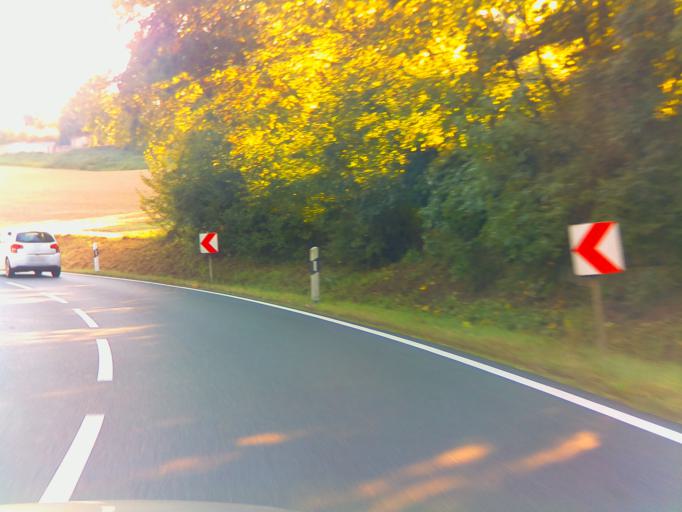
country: DE
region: Bavaria
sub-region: Regierungsbezirk Unterfranken
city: Gaukonigshofen
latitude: 49.6548
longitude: 10.0274
